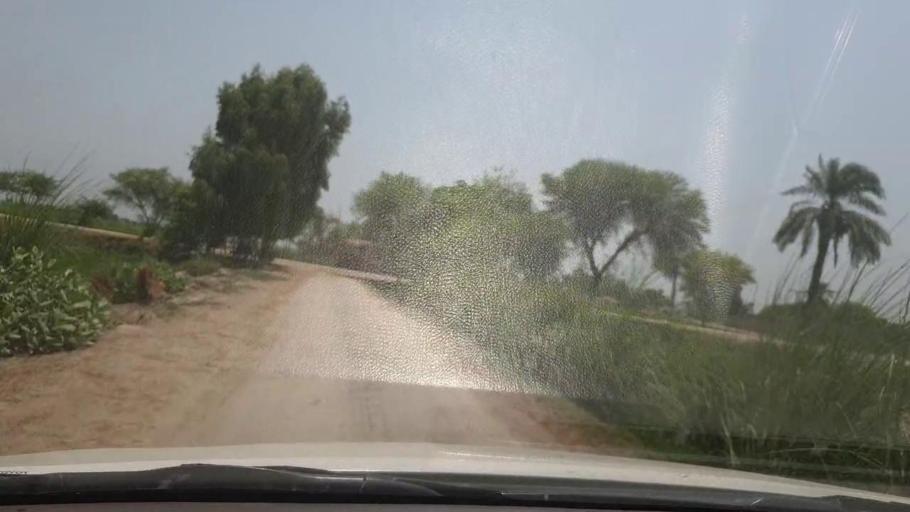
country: PK
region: Sindh
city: Shikarpur
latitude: 28.0701
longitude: 68.5369
